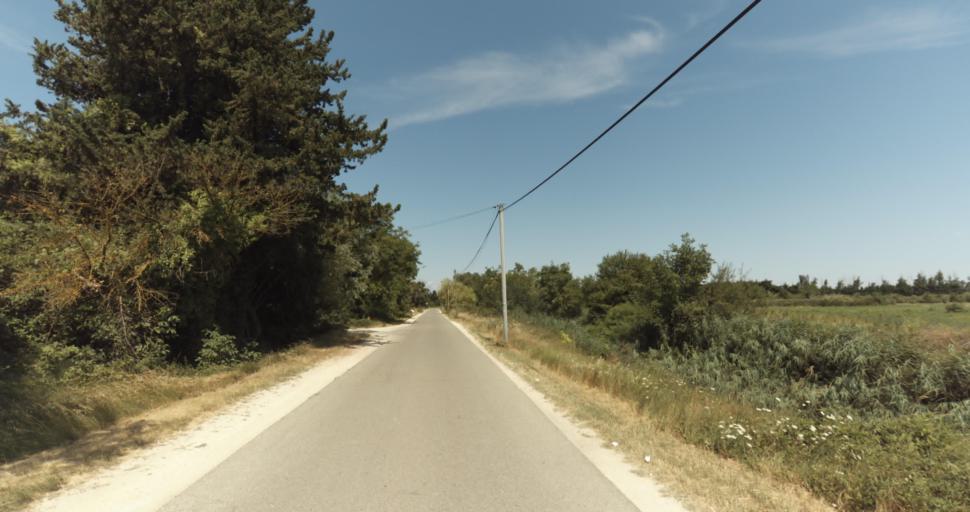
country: FR
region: Provence-Alpes-Cote d'Azur
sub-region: Departement du Vaucluse
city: Monteux
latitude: 44.0184
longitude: 4.9789
